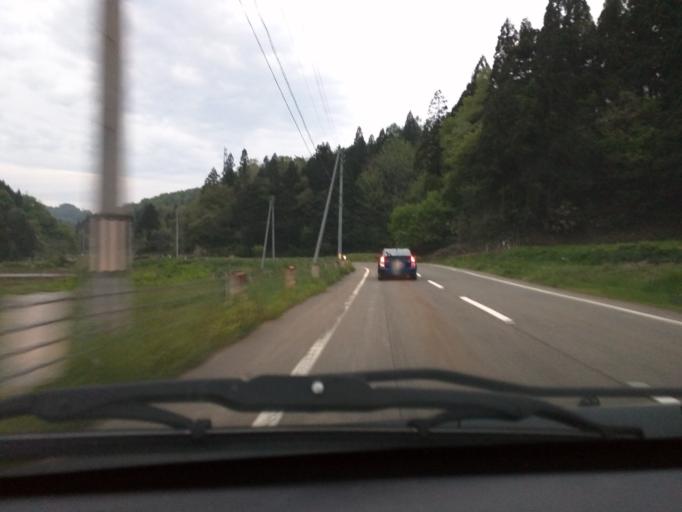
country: JP
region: Niigata
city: Ojiya
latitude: 37.3202
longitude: 138.6968
